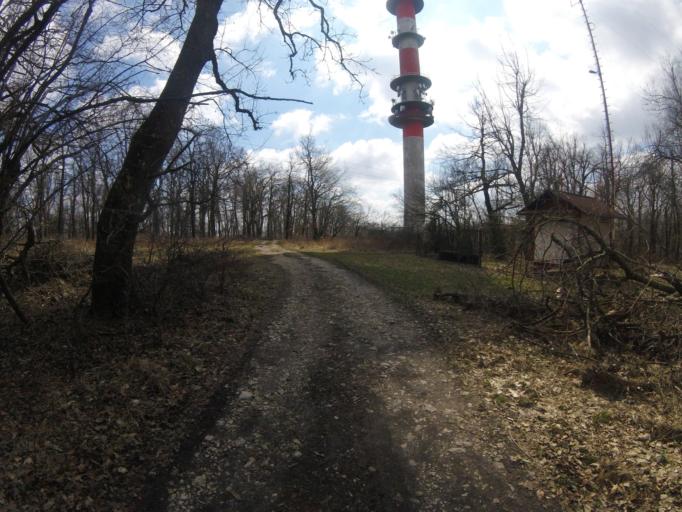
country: HU
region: Komarom-Esztergom
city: Tardos
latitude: 47.6771
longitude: 18.4936
